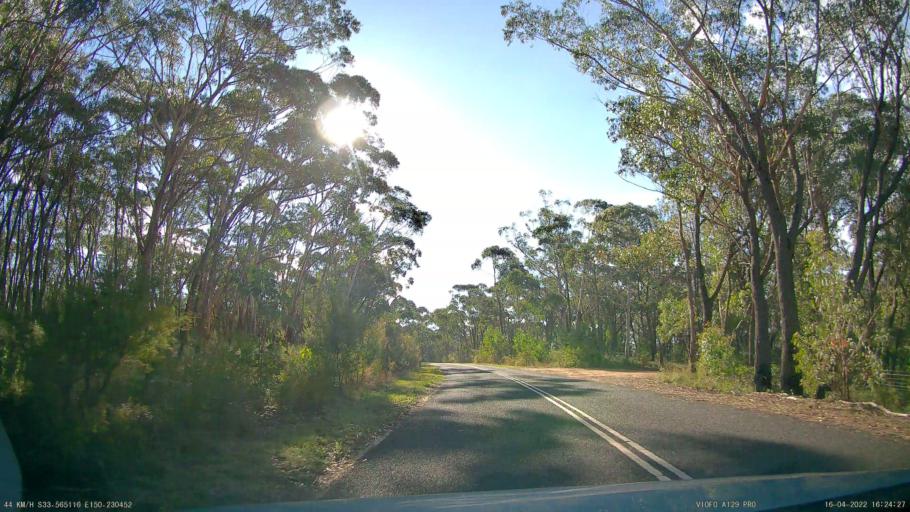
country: AU
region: New South Wales
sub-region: Blue Mountains Municipality
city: Blackheath
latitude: -33.5651
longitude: 150.2304
